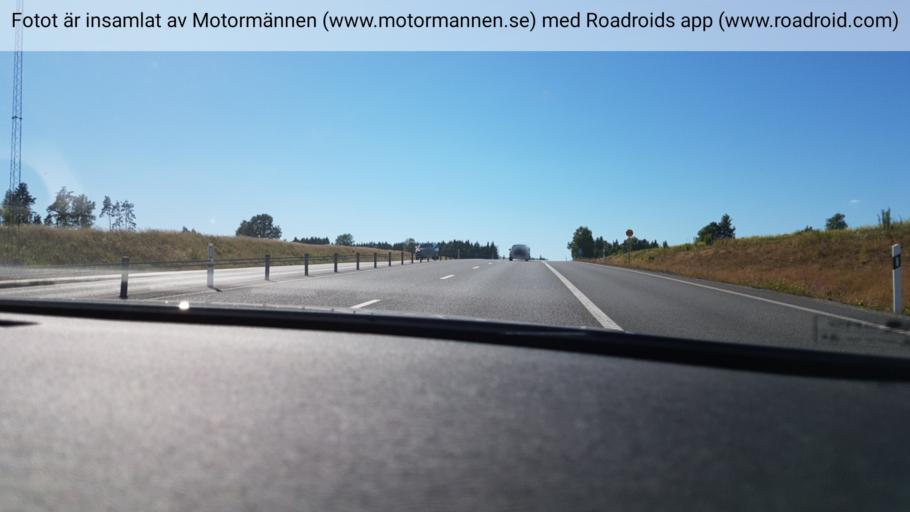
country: SE
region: Joenkoeping
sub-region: Varnamo Kommun
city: Varnamo
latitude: 57.1680
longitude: 14.0310
